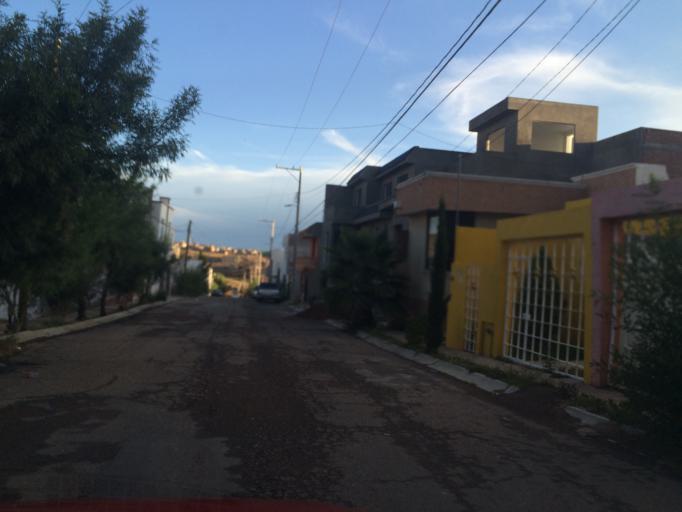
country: MX
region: Zacatecas
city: Zacatecas
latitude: 22.7490
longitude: -102.5833
